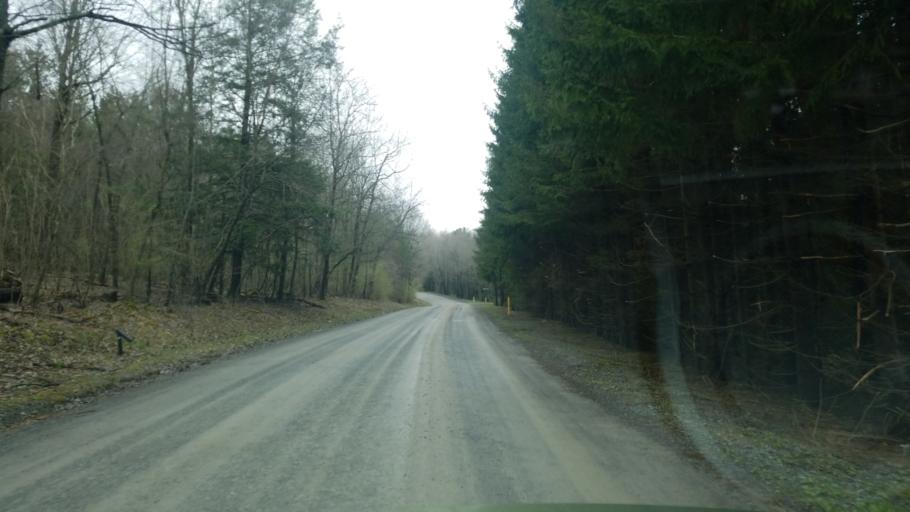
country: US
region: Pennsylvania
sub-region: Clearfield County
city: Shiloh
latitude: 41.1302
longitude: -78.3343
